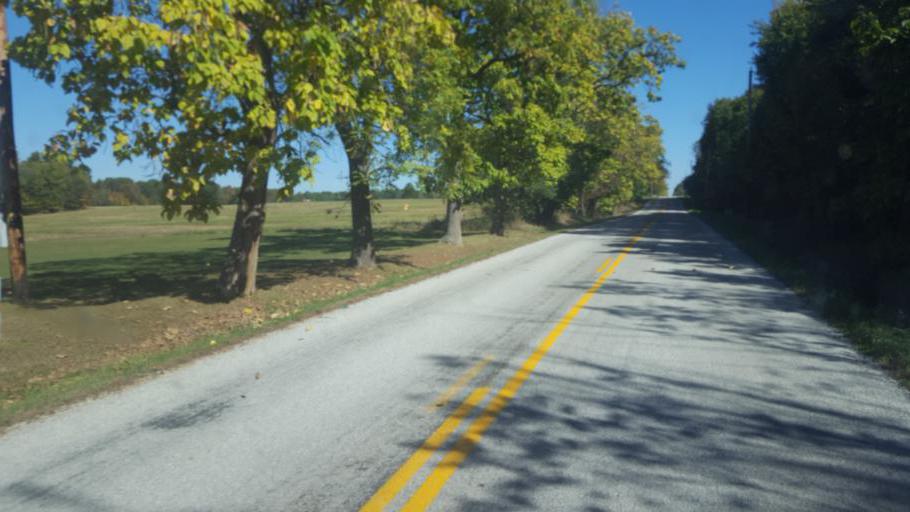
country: US
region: Ohio
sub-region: Ashland County
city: Ashland
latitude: 40.9929
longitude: -82.3044
